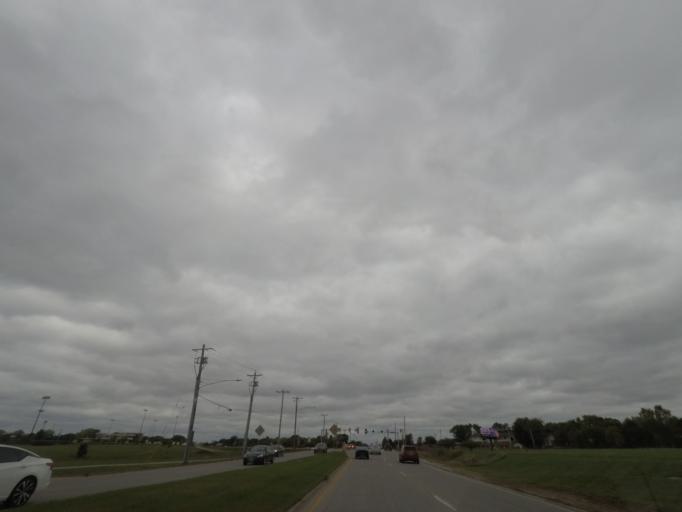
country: US
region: Iowa
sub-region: Polk County
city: Ankeny
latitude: 41.7183
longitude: -93.6004
